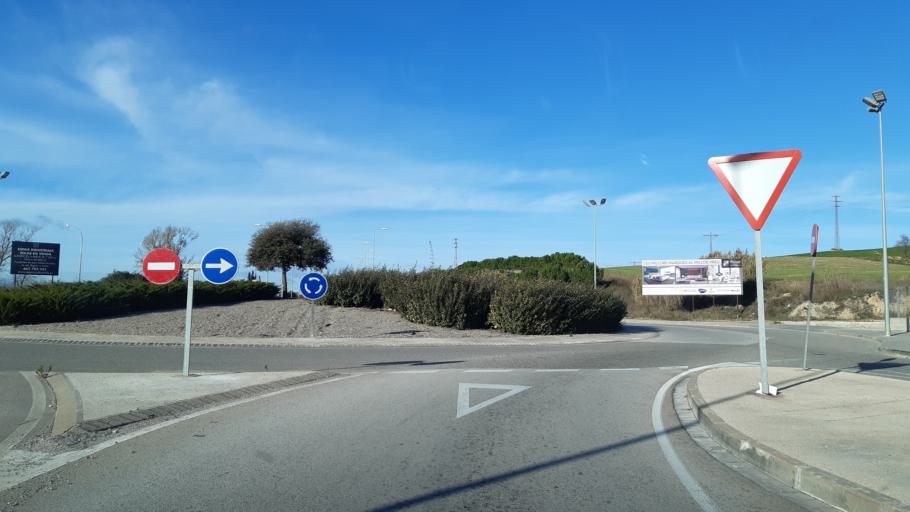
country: ES
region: Catalonia
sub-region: Provincia de Barcelona
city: Vilanova del Cami
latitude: 41.5778
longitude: 1.6503
